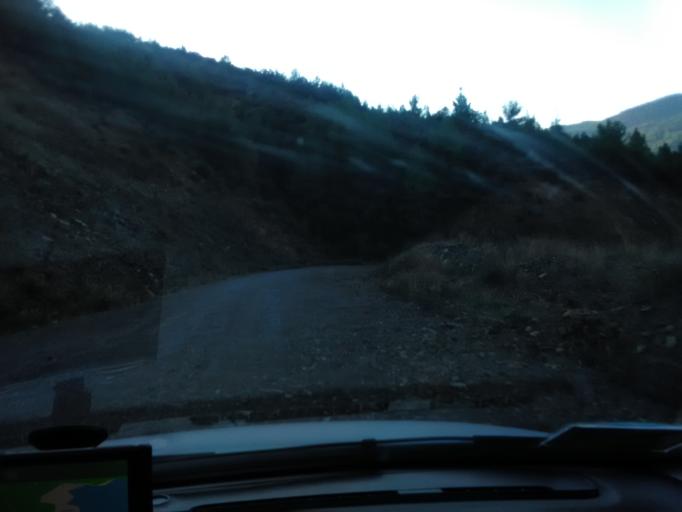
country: TR
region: Antalya
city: Gazipasa
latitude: 36.3109
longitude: 32.3971
